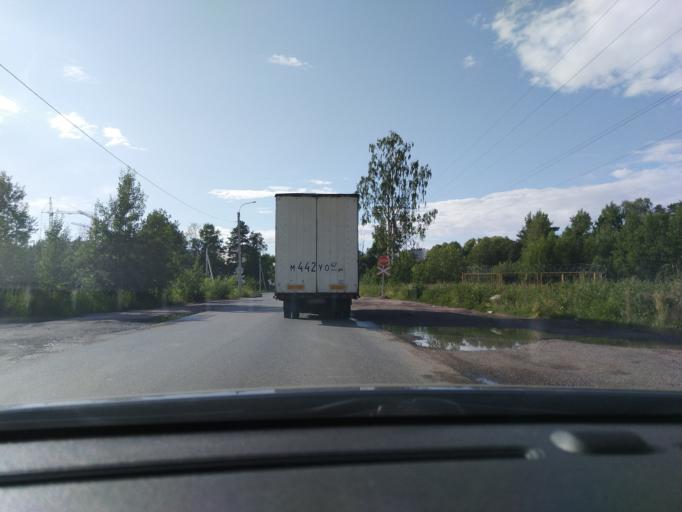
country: RU
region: St.-Petersburg
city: Gorelovo
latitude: 59.7836
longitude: 30.1700
